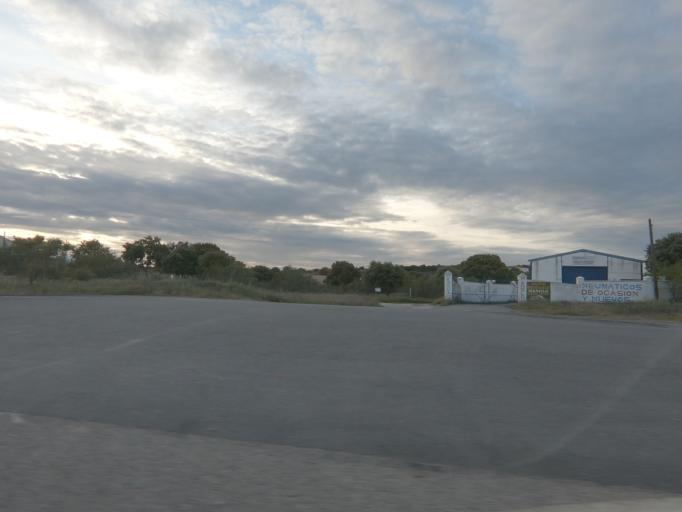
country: ES
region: Extremadura
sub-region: Provincia de Caceres
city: Malpartida de Caceres
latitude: 39.3820
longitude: -6.4443
